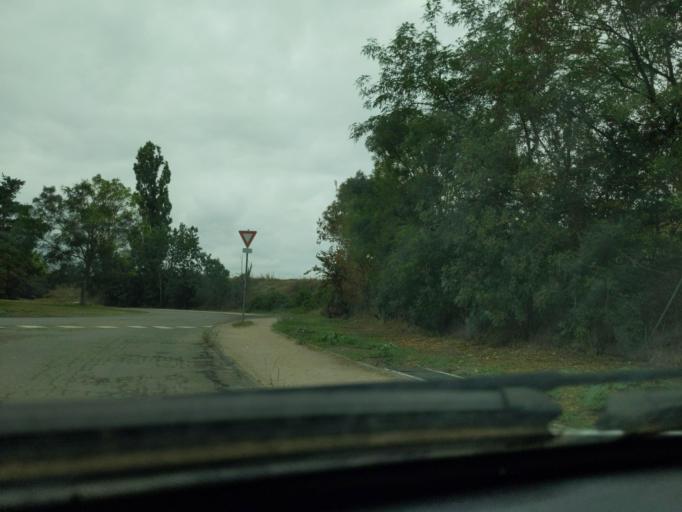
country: FR
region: Midi-Pyrenees
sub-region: Departement de la Haute-Garonne
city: Cugnaux
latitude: 43.5734
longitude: 1.3682
